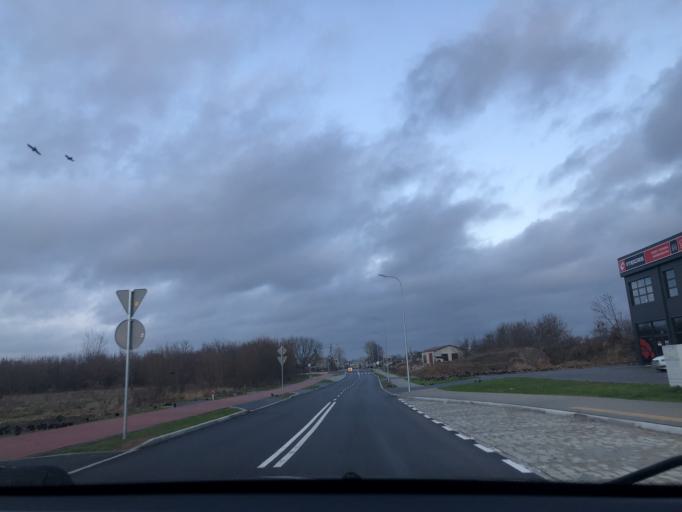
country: PL
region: Podlasie
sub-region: Lomza
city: Lomza
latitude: 53.1697
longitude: 22.0598
